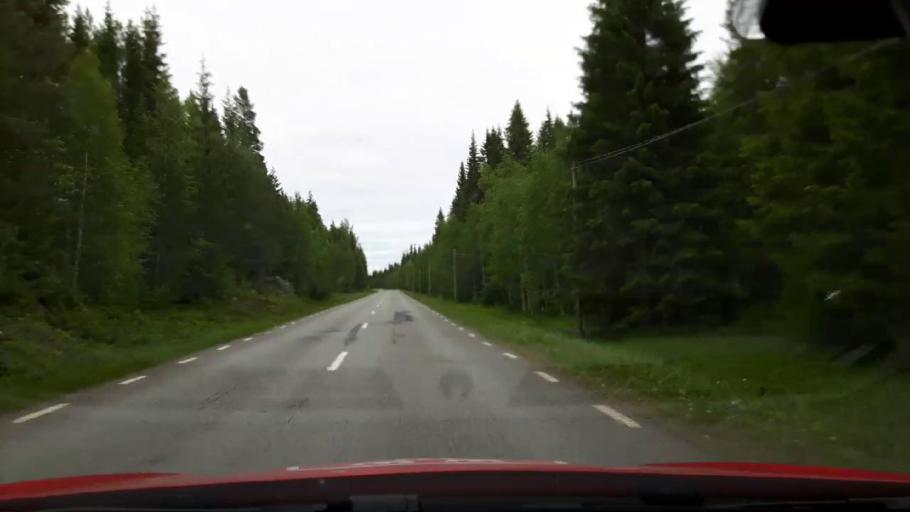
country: SE
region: Jaemtland
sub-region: Stroemsunds Kommun
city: Stroemsund
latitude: 63.4031
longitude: 15.6257
